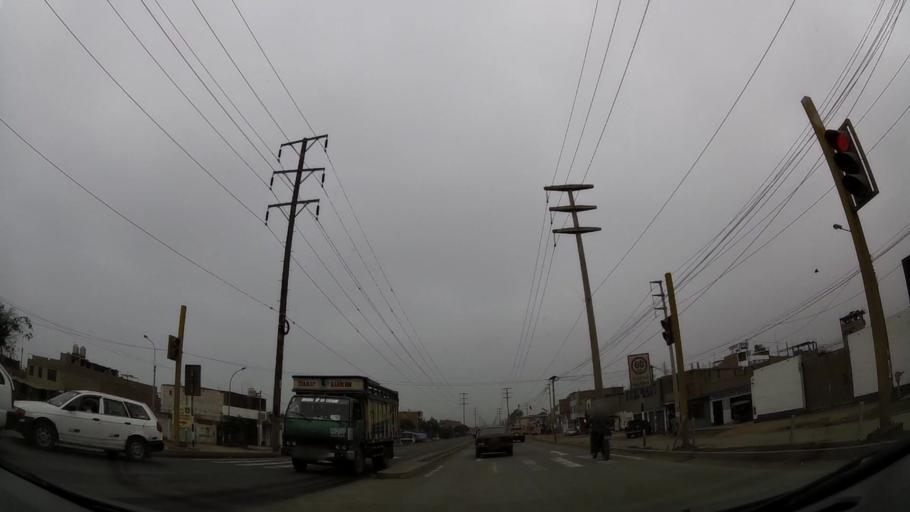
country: PE
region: Lima
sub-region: Lima
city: Punta Hermosa
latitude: -12.2929
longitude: -76.8544
